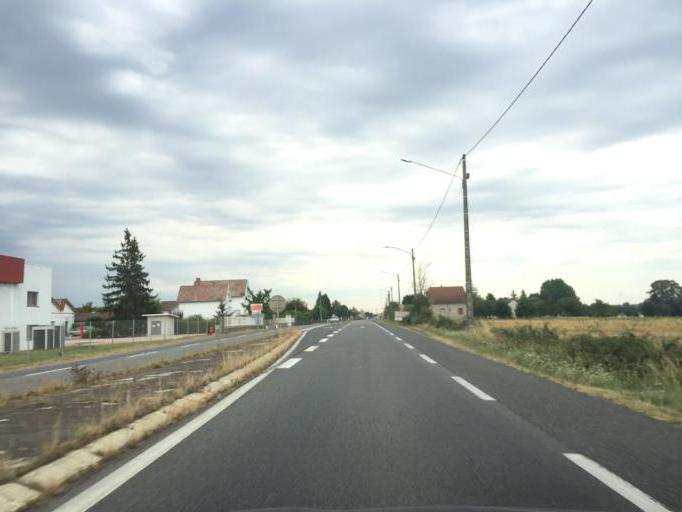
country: FR
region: Auvergne
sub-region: Departement de l'Allier
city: Bessay-sur-Allier
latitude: 46.4499
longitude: 3.3653
